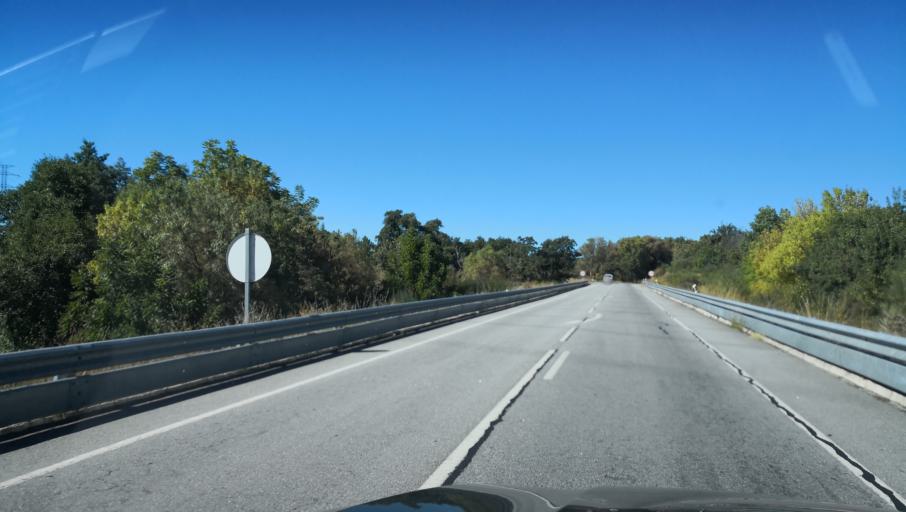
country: PT
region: Vila Real
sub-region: Valpacos
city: Valpacos
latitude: 41.6435
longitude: -7.3187
